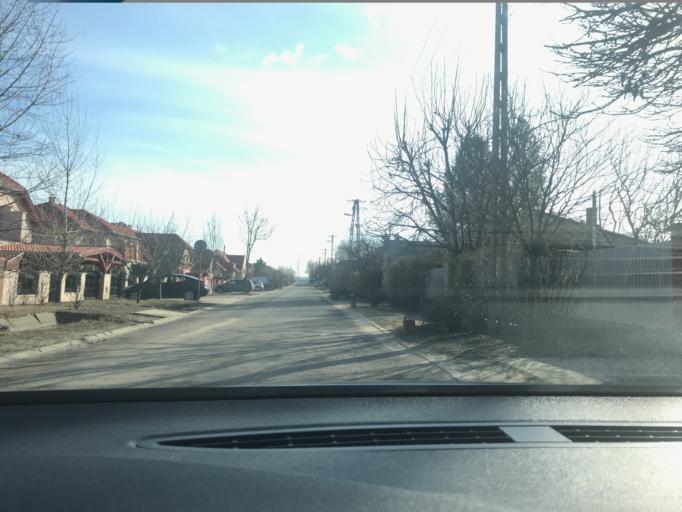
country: HU
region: Pest
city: Dunakeszi
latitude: 47.6294
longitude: 19.1601
